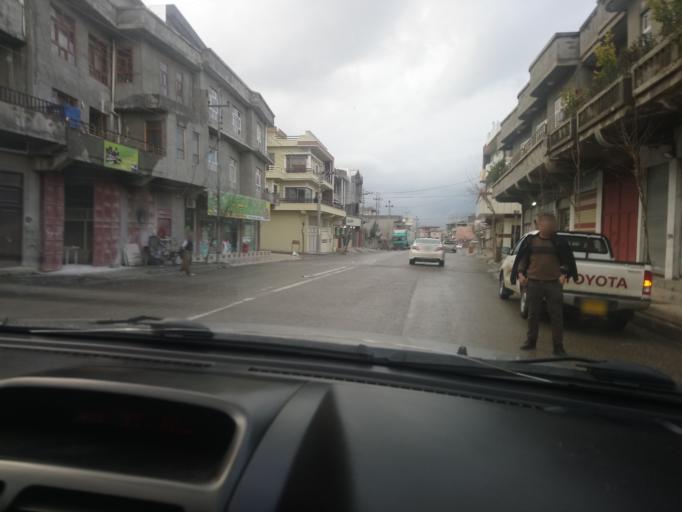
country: IQ
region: As Sulaymaniyah
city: Qeladize
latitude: 36.1839
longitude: 45.1314
